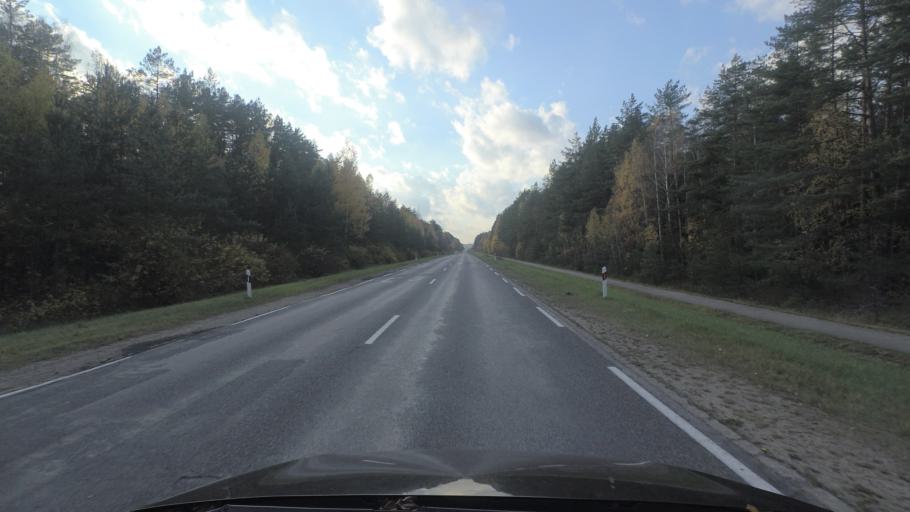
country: LT
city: Pabrade
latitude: 54.9819
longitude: 25.8133
